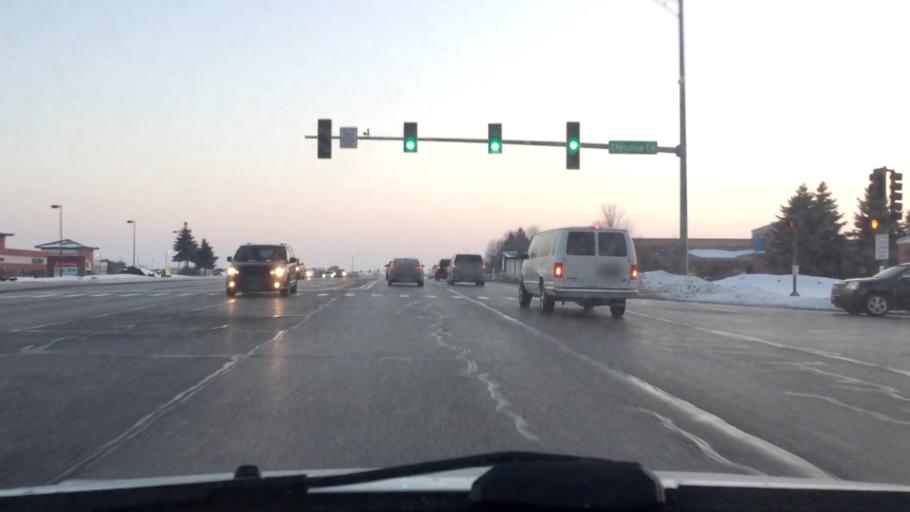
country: US
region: Illinois
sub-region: Kane County
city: Batavia
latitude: 41.8723
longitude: -88.3405
